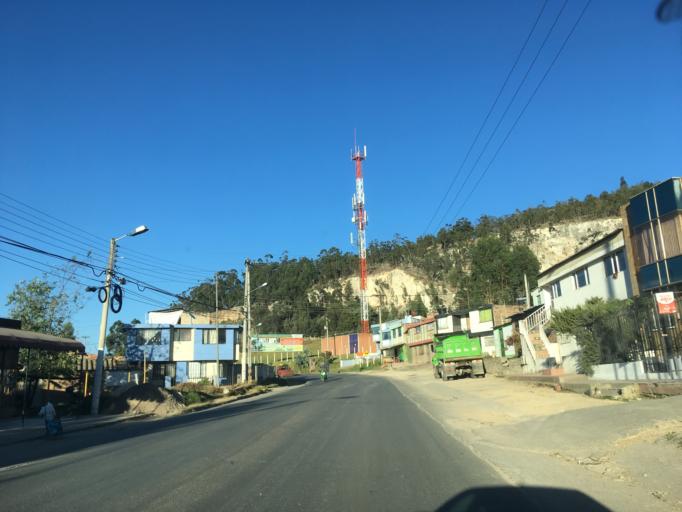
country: CO
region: Boyaca
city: Sogamoso
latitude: 5.6961
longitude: -72.9411
